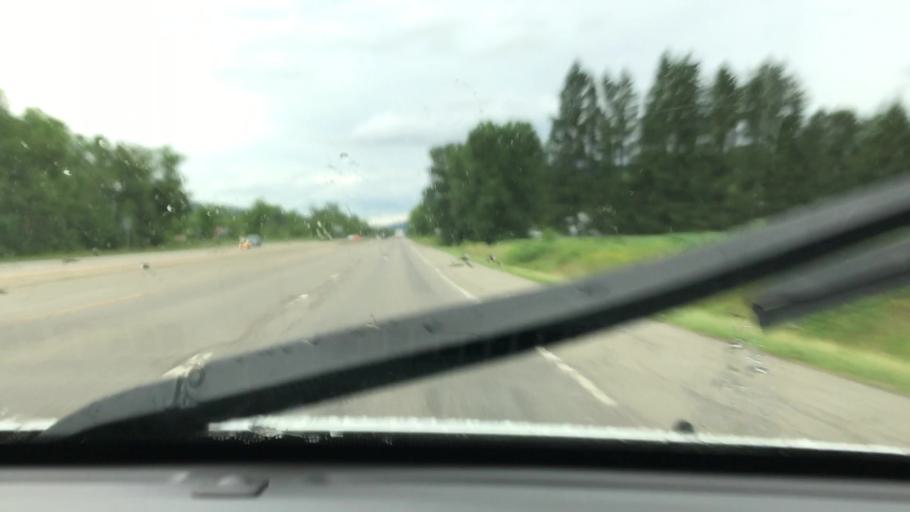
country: US
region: Pennsylvania
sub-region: McKean County
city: Foster Brook
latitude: 42.0364
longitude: -78.6324
